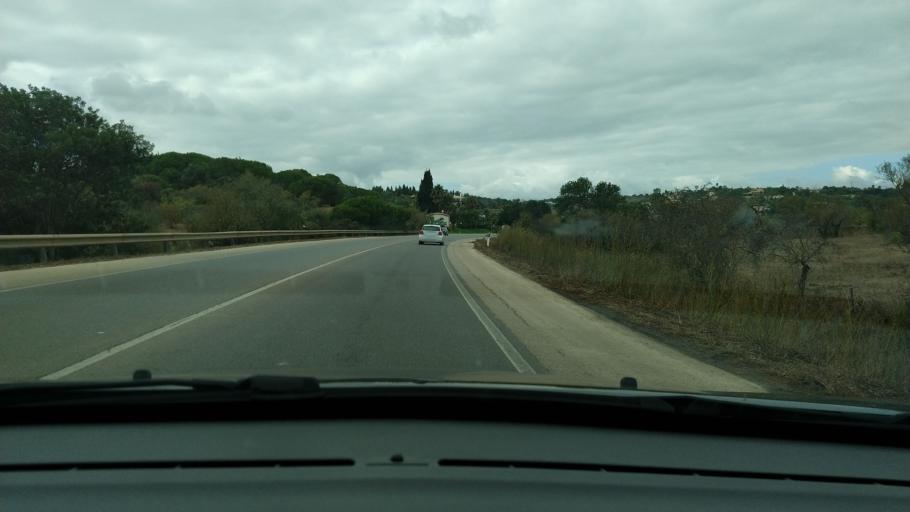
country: PT
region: Faro
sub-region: Lagos
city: Lagos
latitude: 37.1026
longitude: -8.7006
